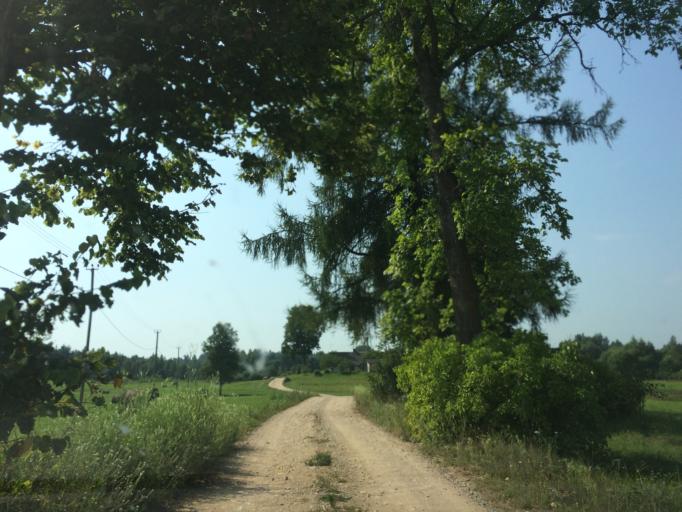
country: LV
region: Ludzas Rajons
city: Ludza
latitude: 56.5417
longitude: 27.5853
